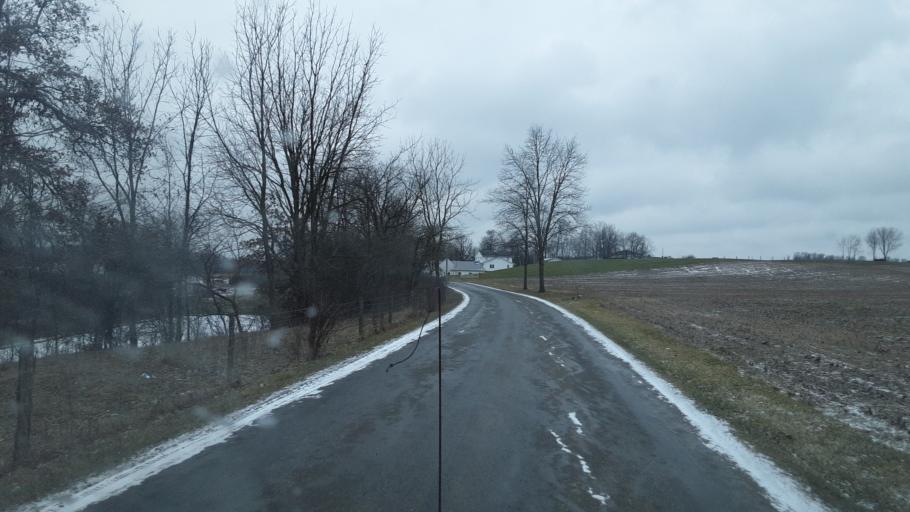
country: US
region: Ohio
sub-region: Wayne County
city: Apple Creek
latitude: 40.6246
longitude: -81.7500
